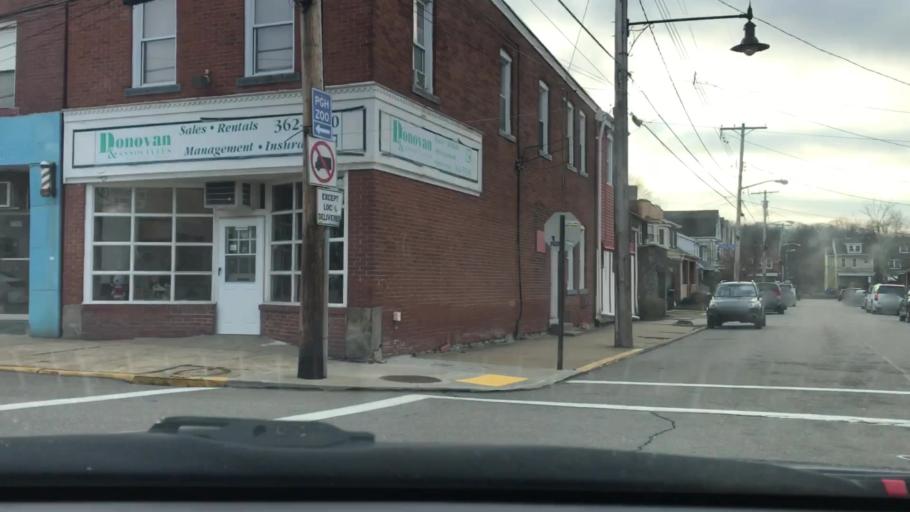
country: US
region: Pennsylvania
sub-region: Allegheny County
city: Sharpsburg
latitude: 40.4865
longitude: -79.9257
